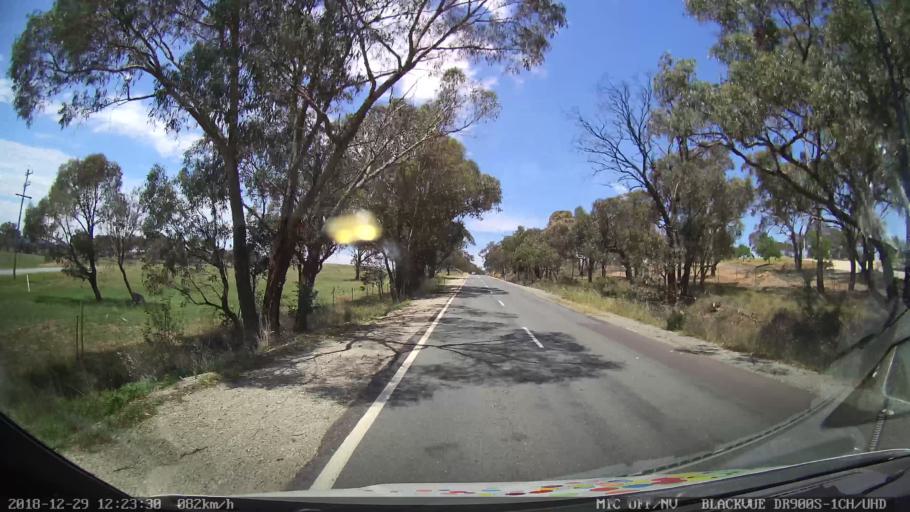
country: AU
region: New South Wales
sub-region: Queanbeyan
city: Queanbeyan
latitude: -35.4371
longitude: 149.2162
